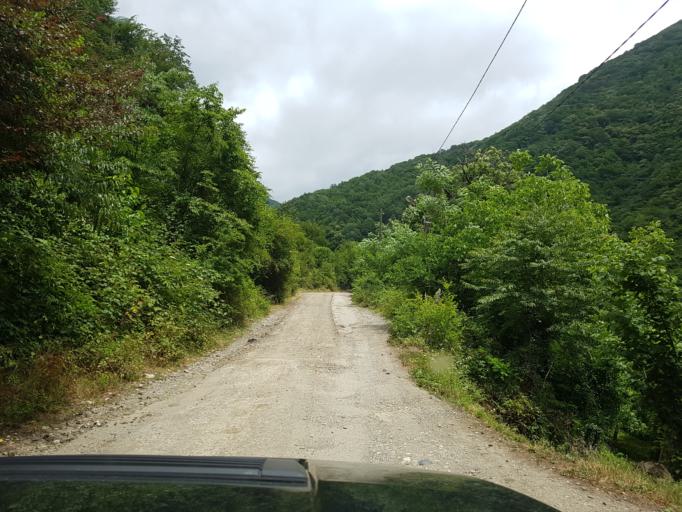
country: GE
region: Imereti
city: Kutaisi
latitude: 42.4373
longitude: 42.7548
